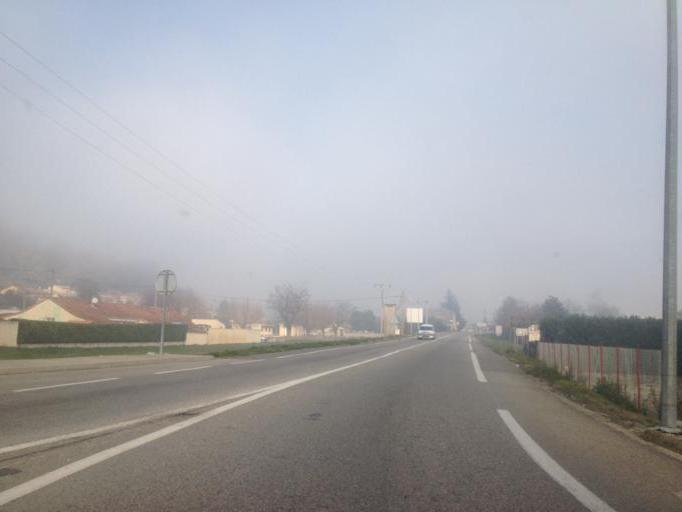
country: FR
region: Rhone-Alpes
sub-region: Departement de l'Ardeche
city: Meysse
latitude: 44.6040
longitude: 4.7195
